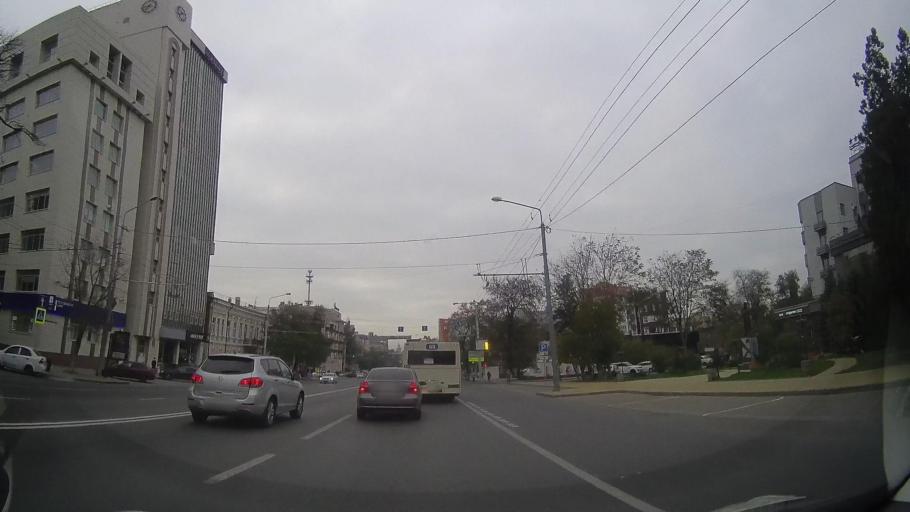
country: RU
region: Rostov
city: Rostov-na-Donu
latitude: 47.2274
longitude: 39.7043
